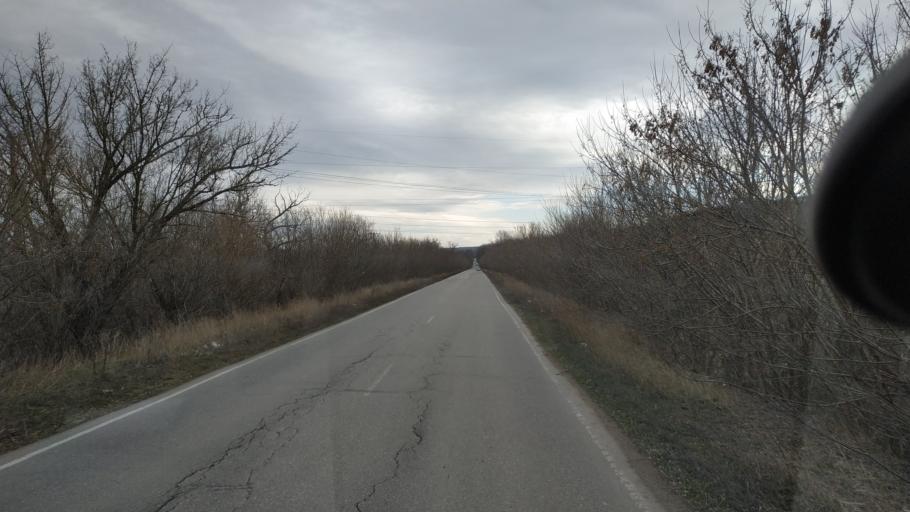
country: MD
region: Chisinau
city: Vadul lui Voda
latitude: 47.1119
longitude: 29.0598
